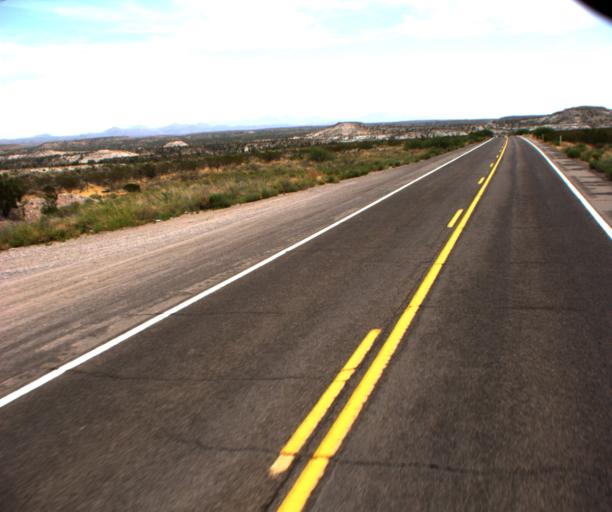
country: US
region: Arizona
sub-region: Graham County
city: Bylas
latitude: 33.2448
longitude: -110.2663
